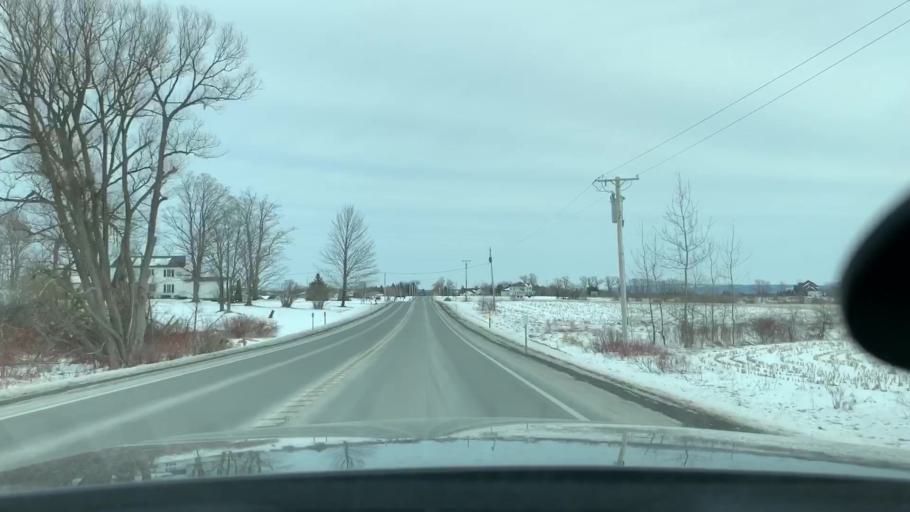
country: US
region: New York
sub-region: Herkimer County
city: Frankfort
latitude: 43.0332
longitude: -75.1173
